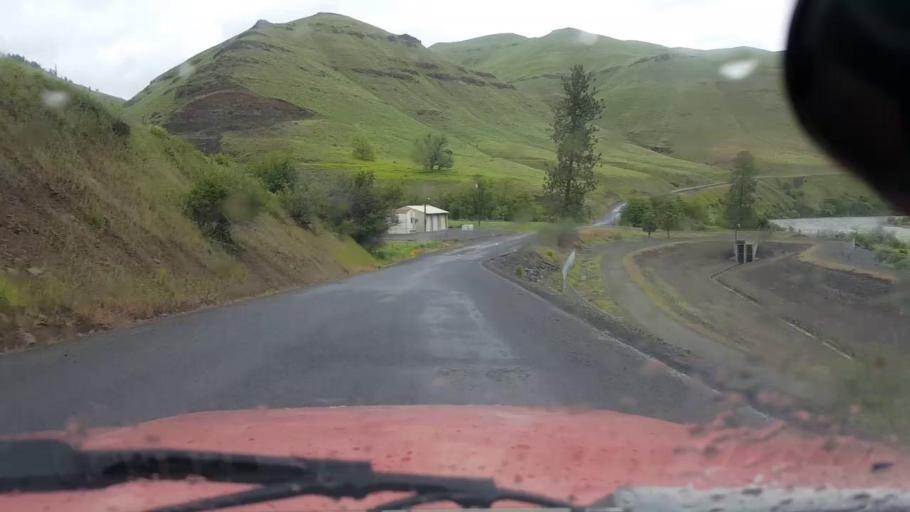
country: US
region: Washington
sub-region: Asotin County
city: Asotin
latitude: 46.0371
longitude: -117.2974
